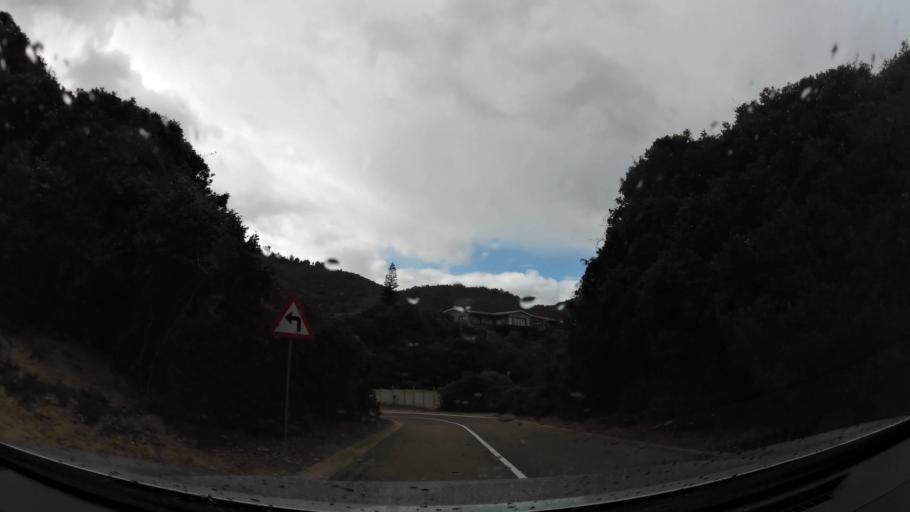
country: ZA
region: Western Cape
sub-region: Eden District Municipality
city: George
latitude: -34.0494
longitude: 22.3107
